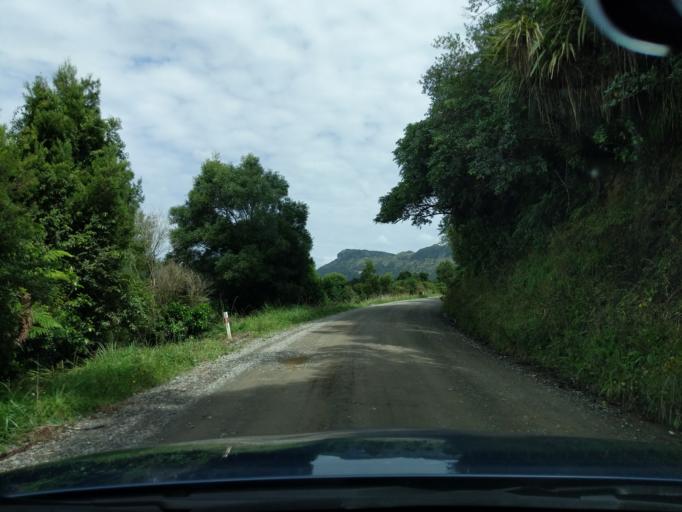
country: NZ
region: Tasman
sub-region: Tasman District
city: Takaka
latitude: -40.6498
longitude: 172.4690
